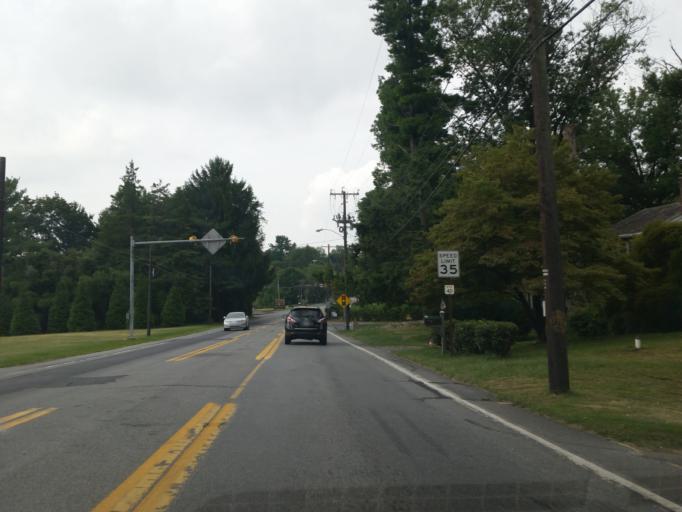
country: US
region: Pennsylvania
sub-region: Lancaster County
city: East Petersburg
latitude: 40.0907
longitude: -76.3042
